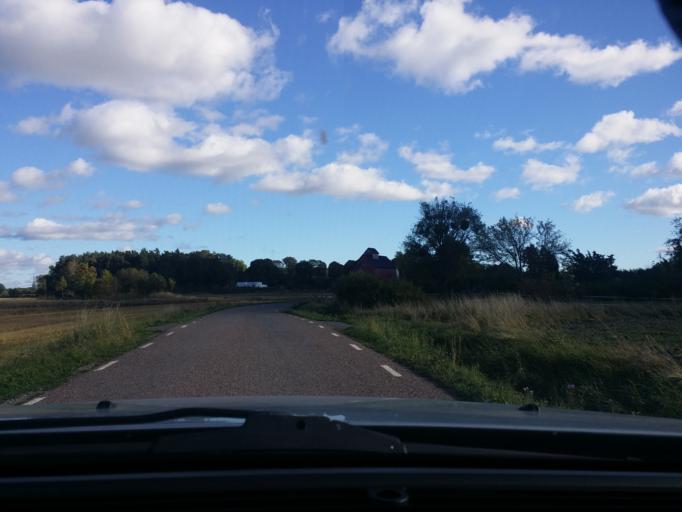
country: SE
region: Vaestmanland
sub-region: Vasteras
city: Vasteras
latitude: 59.5383
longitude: 16.4728
